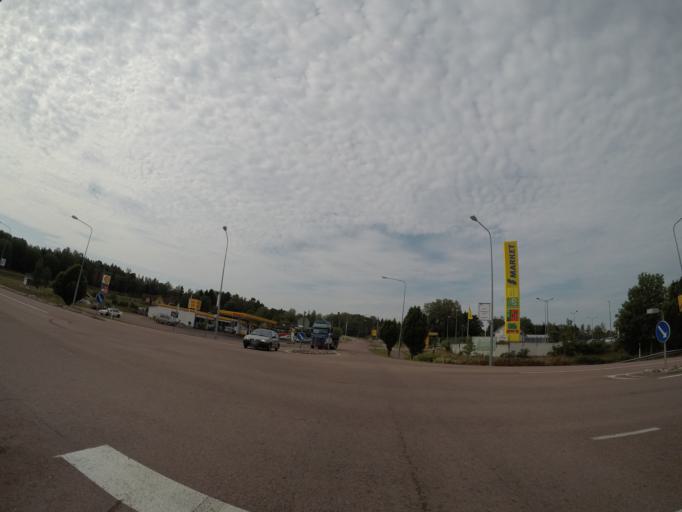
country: AX
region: Alands landsbygd
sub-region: Finstroem
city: Finstroem
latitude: 60.2301
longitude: 19.9882
